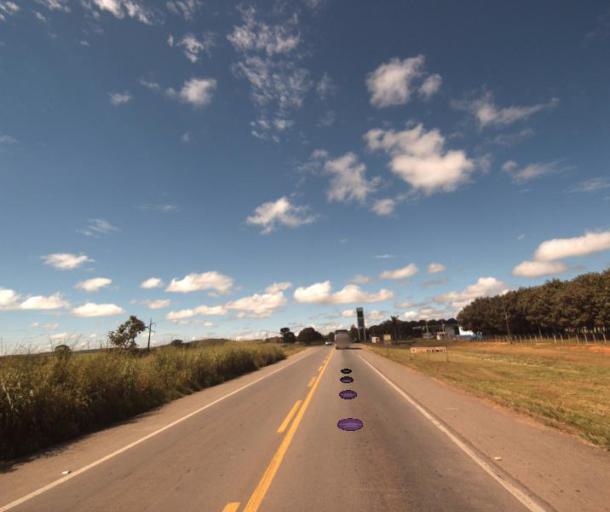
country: BR
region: Goias
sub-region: Rialma
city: Rialma
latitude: -15.4667
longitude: -49.4988
